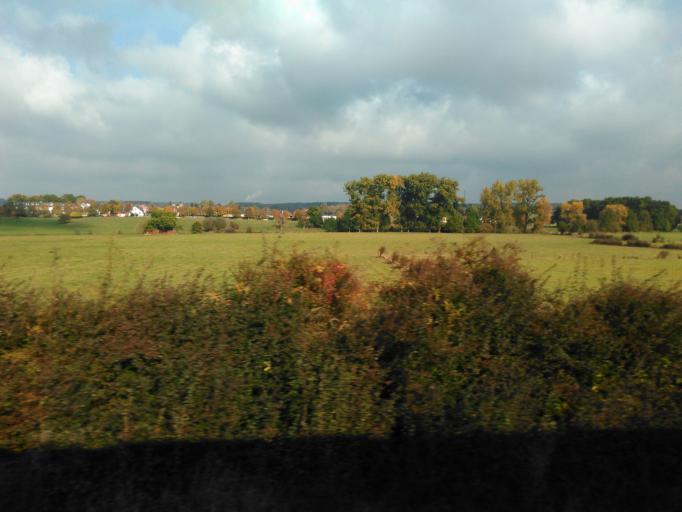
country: LU
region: Luxembourg
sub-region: Canton d'Esch-sur-Alzette
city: Bettembourg
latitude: 49.5151
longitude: 6.0840
